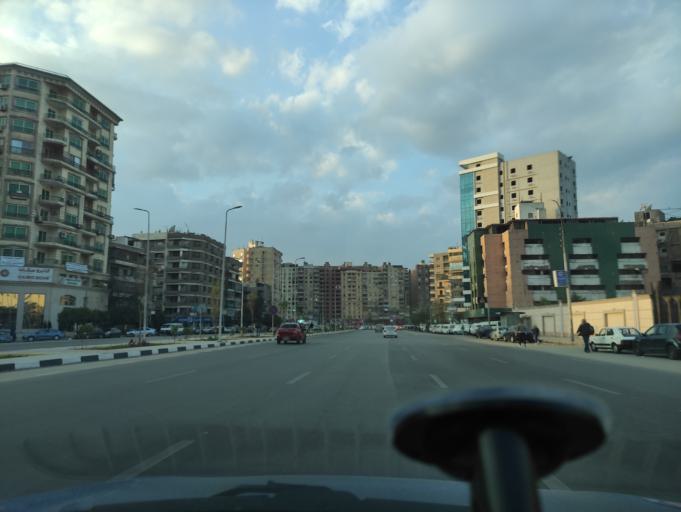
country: EG
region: Muhafazat al Qalyubiyah
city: Al Khankah
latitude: 30.1168
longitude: 31.3421
